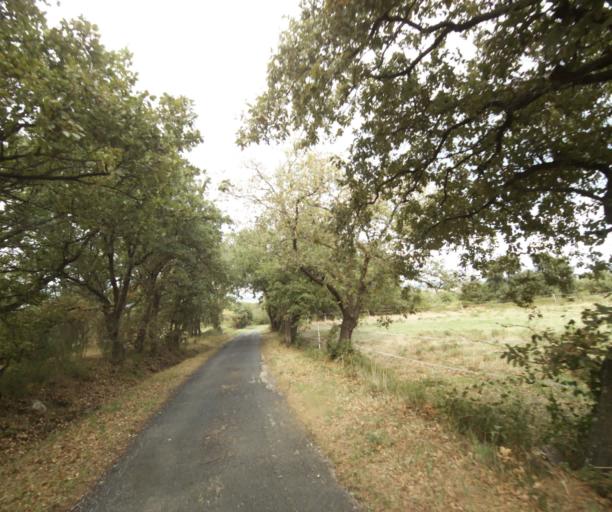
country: FR
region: Languedoc-Roussillon
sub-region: Departement des Pyrenees-Orientales
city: Argelers
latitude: 42.5290
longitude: 3.0091
